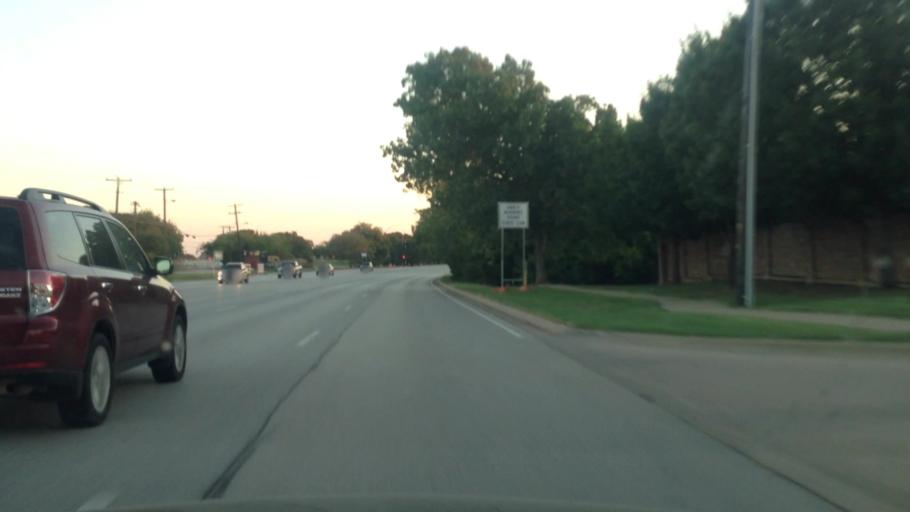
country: US
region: Texas
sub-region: Tarrant County
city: North Richland Hills
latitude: 32.8562
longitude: -97.2122
